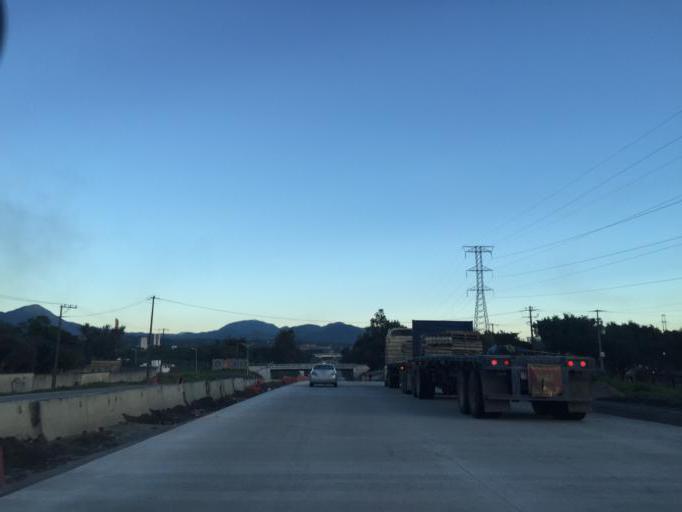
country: MX
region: Veracruz
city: Ixtac Zoquitlan
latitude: 18.8560
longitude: -97.0694
